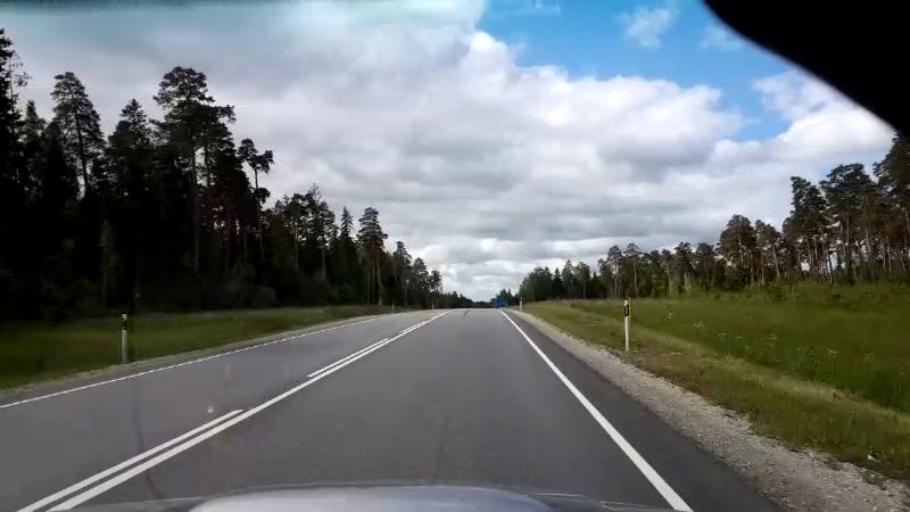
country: EE
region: Raplamaa
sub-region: Maerjamaa vald
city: Marjamaa
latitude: 58.9323
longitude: 24.4627
